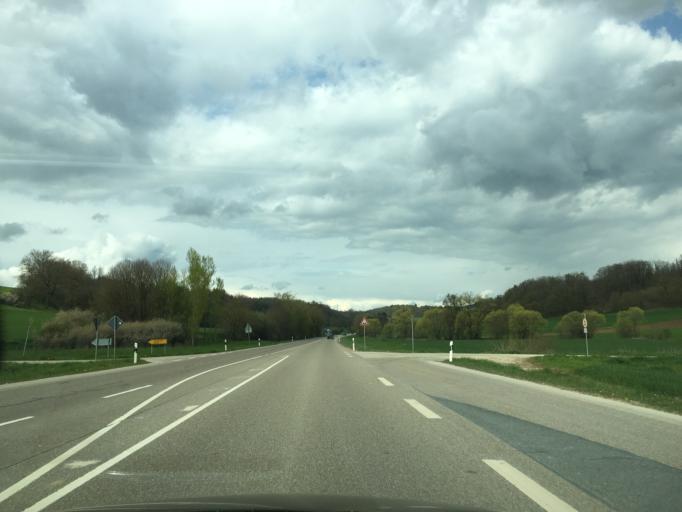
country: DE
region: Bavaria
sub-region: Regierungsbezirk Mittelfranken
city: Langenaltheim
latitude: 48.9253
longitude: 10.9169
